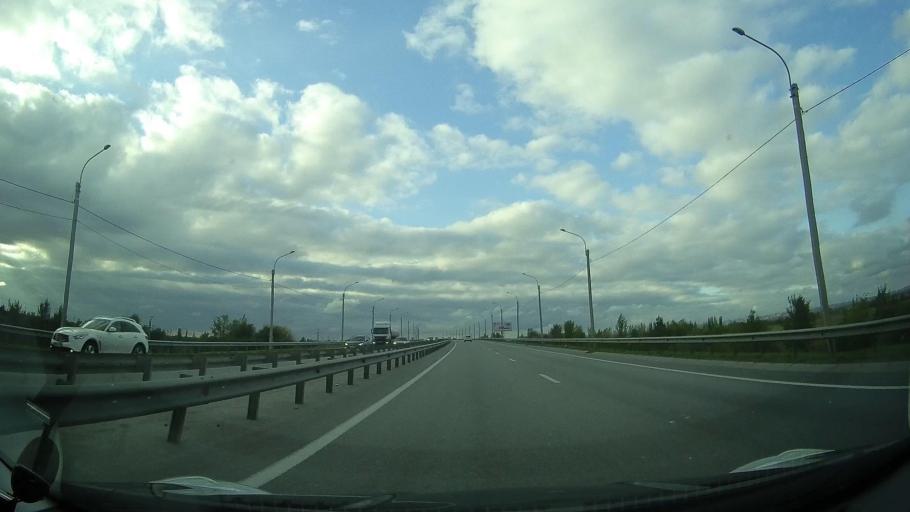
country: RU
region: Rostov
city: Bataysk
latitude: 47.1609
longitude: 39.7641
